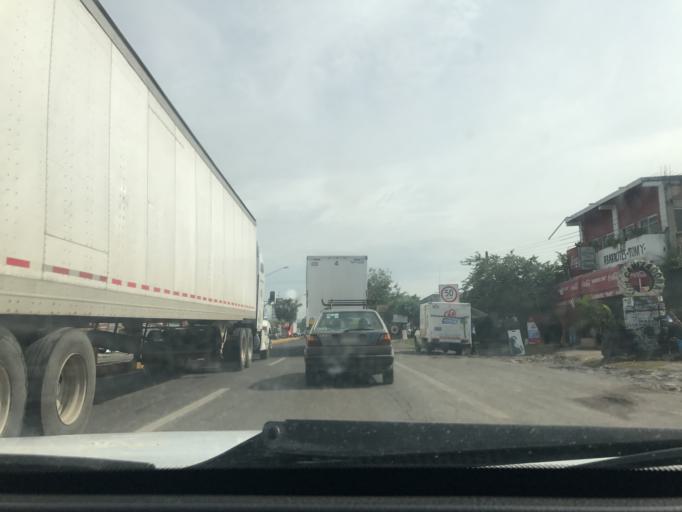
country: MX
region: Morelos
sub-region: Cuautla
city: Tierra Larga (Campo Nuevo)
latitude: 18.8602
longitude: -98.9335
